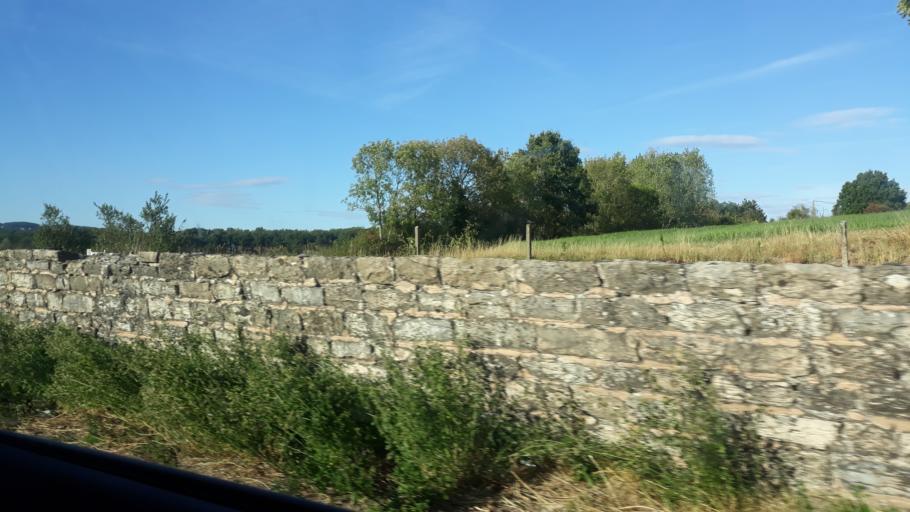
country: FR
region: Bourgogne
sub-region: Departement de Saone-et-Loire
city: Torcy
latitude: 46.7735
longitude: 4.4480
